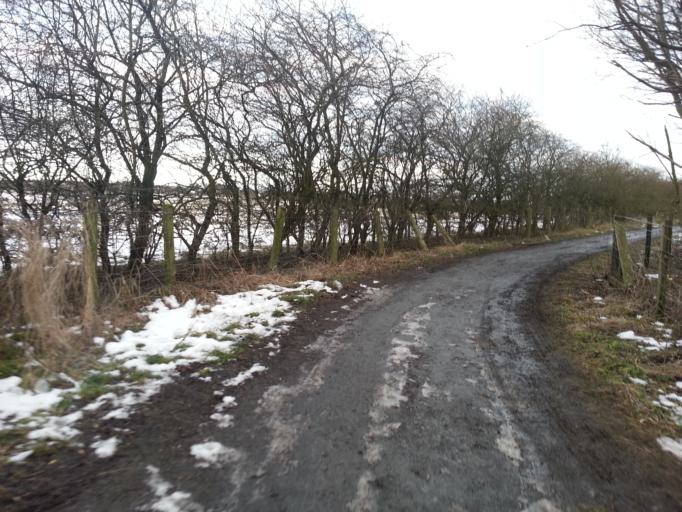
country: GB
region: England
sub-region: County Durham
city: Crook
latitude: 54.7243
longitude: -1.7534
